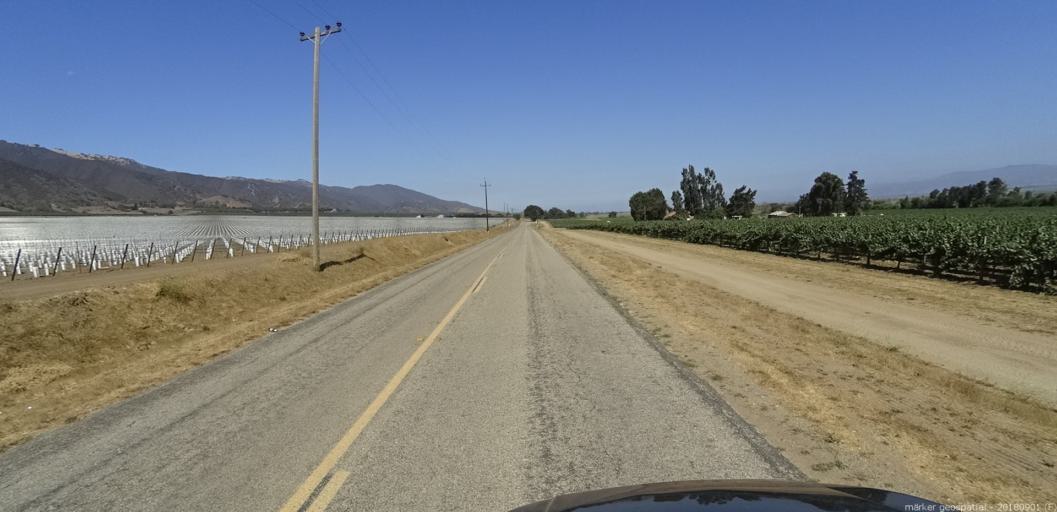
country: US
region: California
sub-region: Monterey County
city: Gonzales
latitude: 36.4898
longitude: -121.4922
